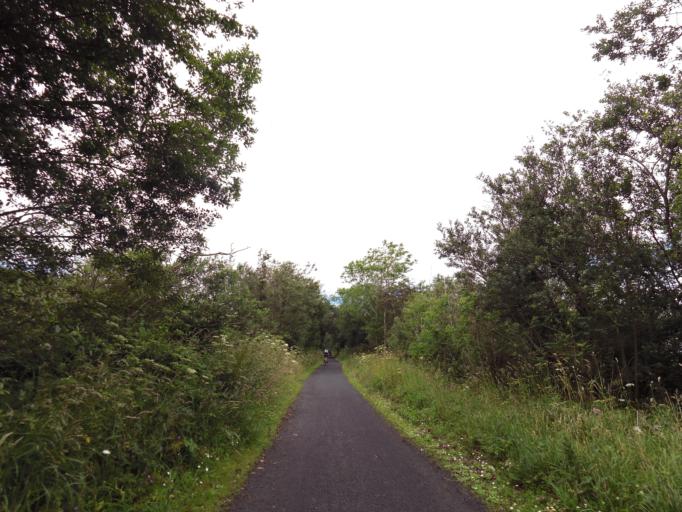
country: IE
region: Connaught
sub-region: Maigh Eo
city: Westport
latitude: 53.8169
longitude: -9.5362
